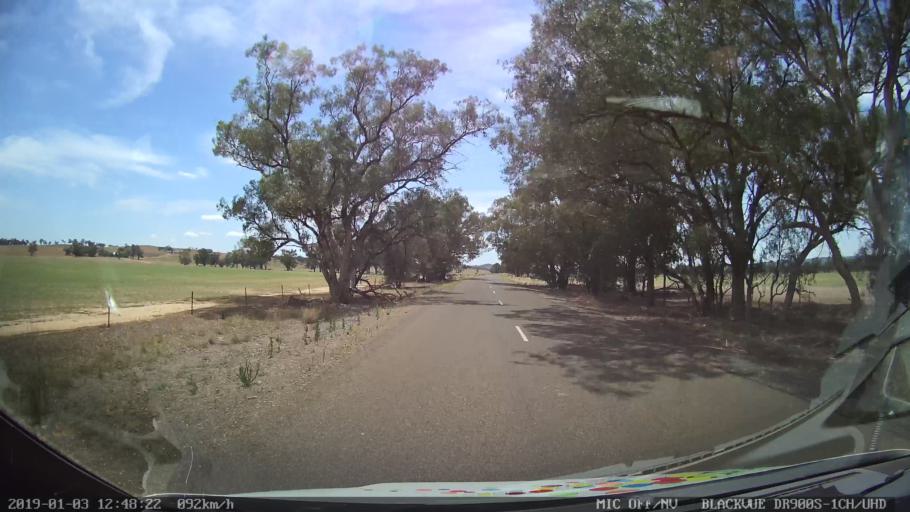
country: AU
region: New South Wales
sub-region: Weddin
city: Grenfell
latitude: -33.7153
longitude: 148.2499
